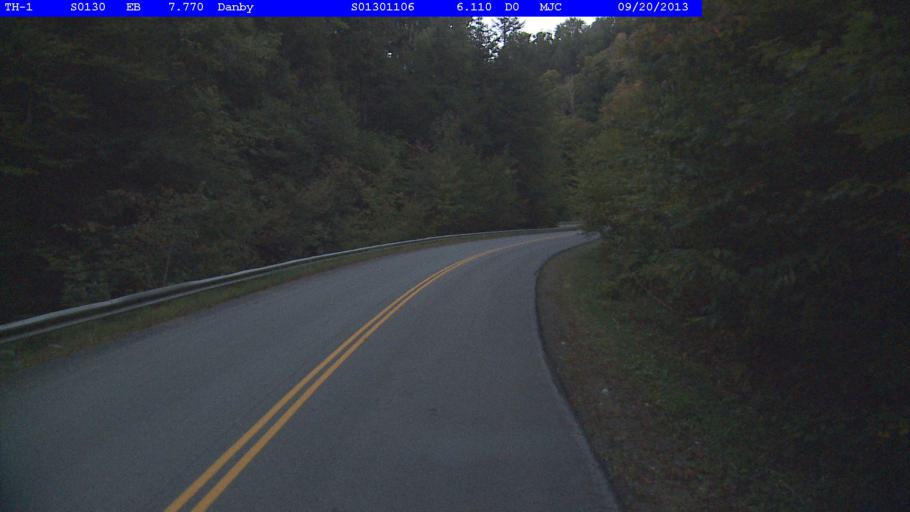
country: US
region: Vermont
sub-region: Bennington County
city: Manchester Center
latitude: 43.3421
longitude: -73.0301
